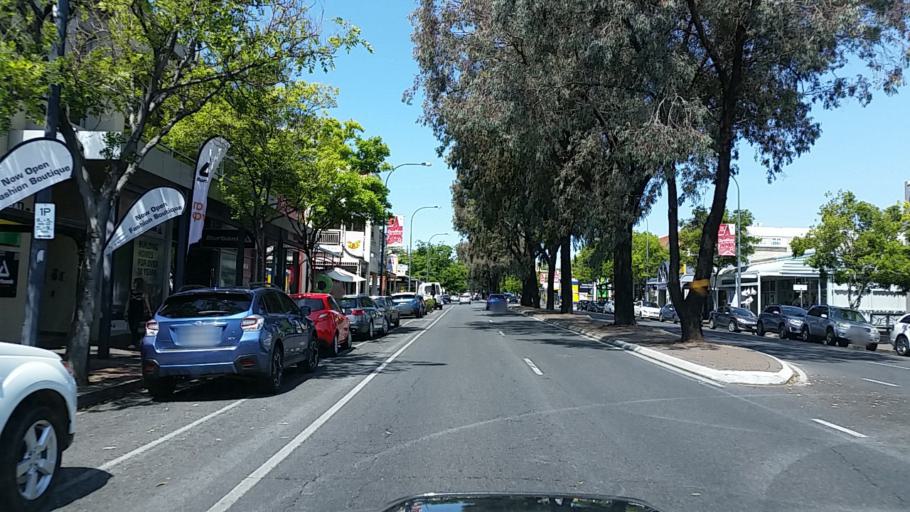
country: AU
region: South Australia
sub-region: Norwood Payneham St Peters
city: Trinity Gardens
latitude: -34.9215
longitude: 138.6285
